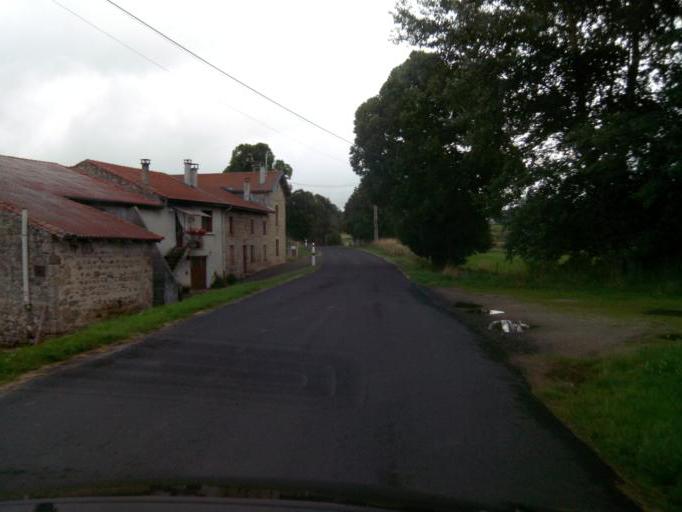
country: FR
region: Rhone-Alpes
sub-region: Departement de la Loire
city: Saint-Bonnet-le-Chateau
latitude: 45.3944
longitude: 4.0171
